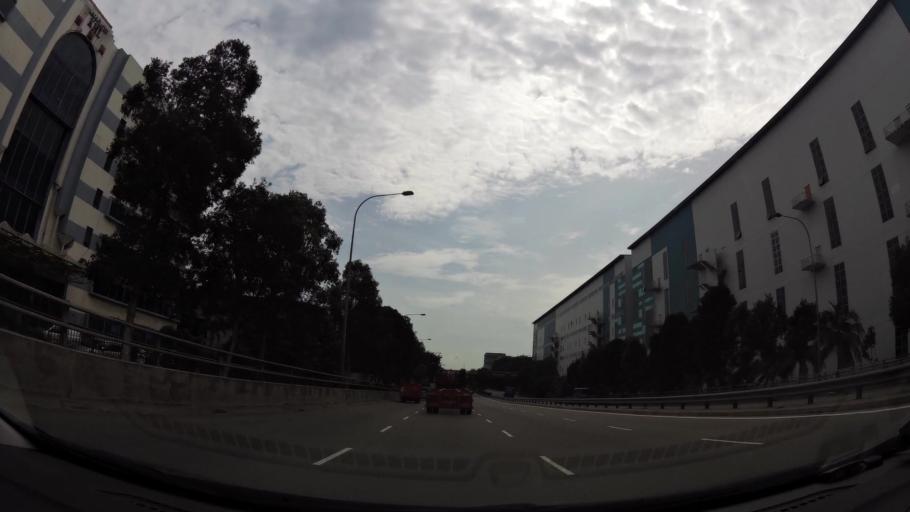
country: SG
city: Singapore
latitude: 1.3126
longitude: 103.7284
